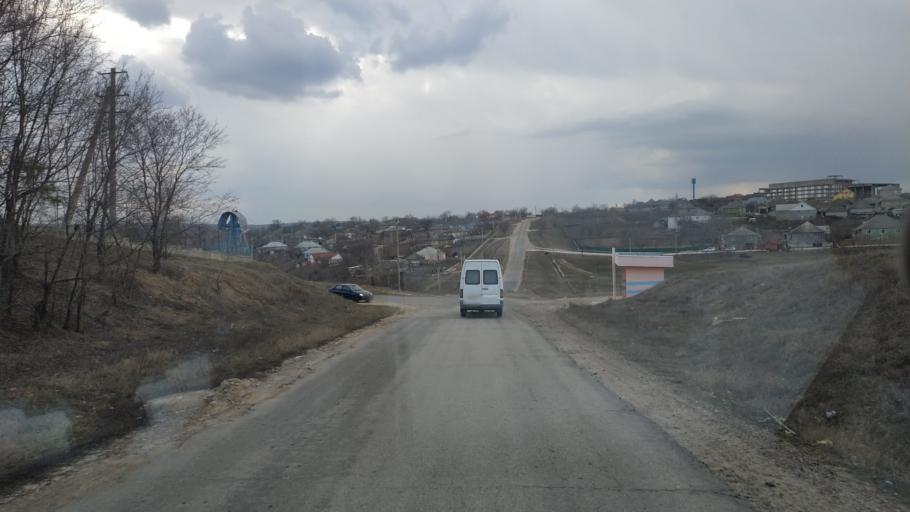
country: MD
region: Anenii Noi
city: Anenii Noi
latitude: 46.9073
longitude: 29.3230
